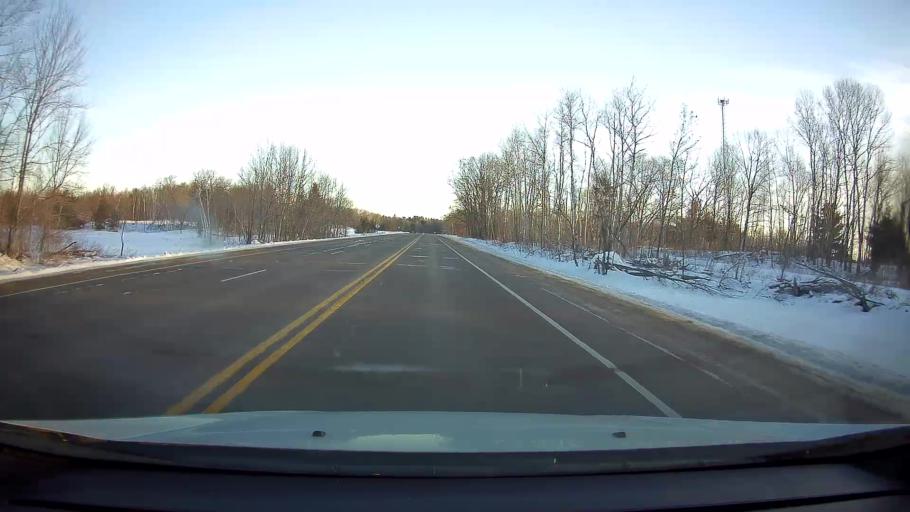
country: US
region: Wisconsin
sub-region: Barron County
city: Turtle Lake
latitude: 45.4497
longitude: -92.1080
